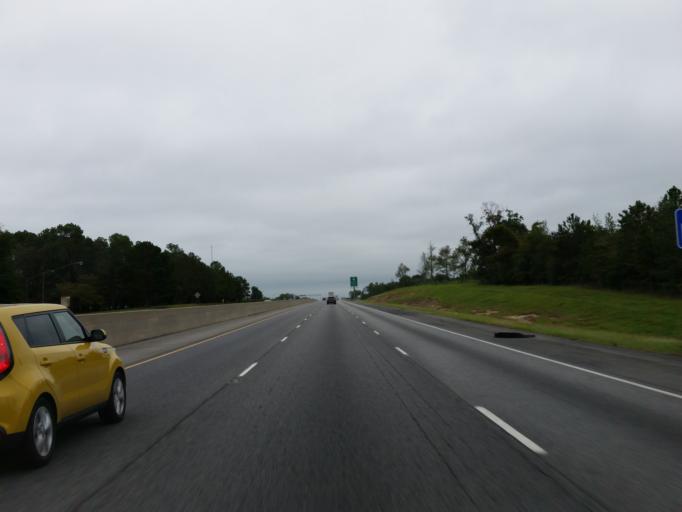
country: US
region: Georgia
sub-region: Turner County
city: Ashburn
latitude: 31.7529
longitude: -83.6649
